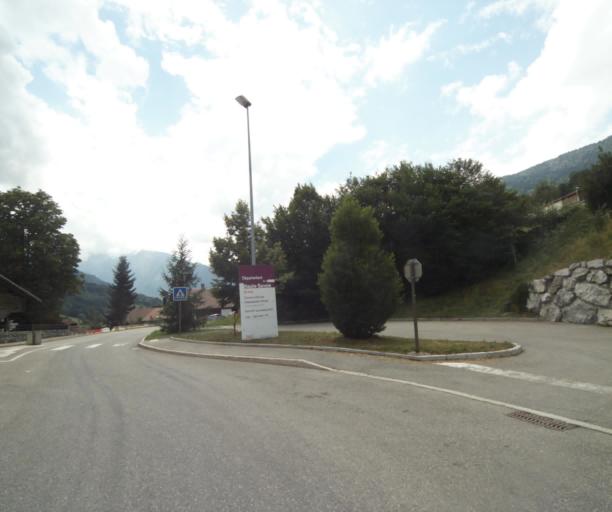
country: FR
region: Rhone-Alpes
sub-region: Departement de la Haute-Savoie
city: Saint-Jean-de-Sixt
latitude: 45.9082
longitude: 6.3651
